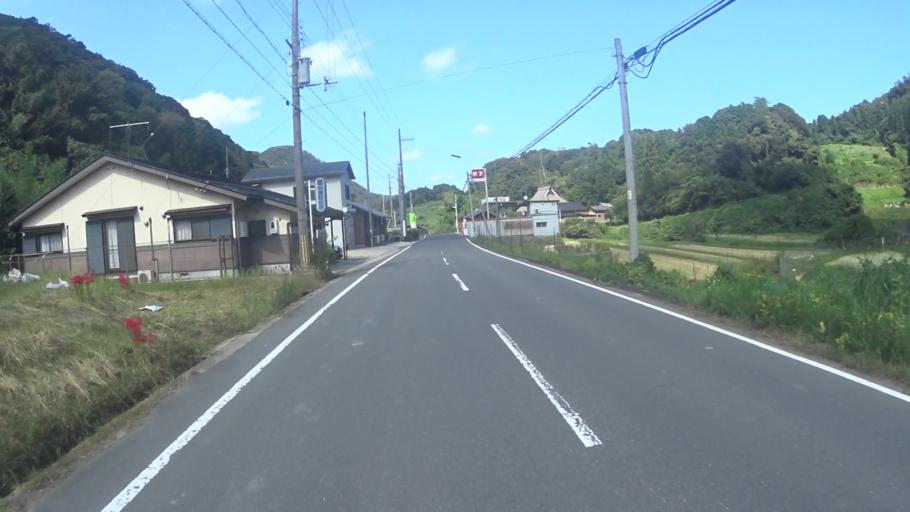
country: JP
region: Kyoto
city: Miyazu
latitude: 35.6951
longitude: 135.2777
